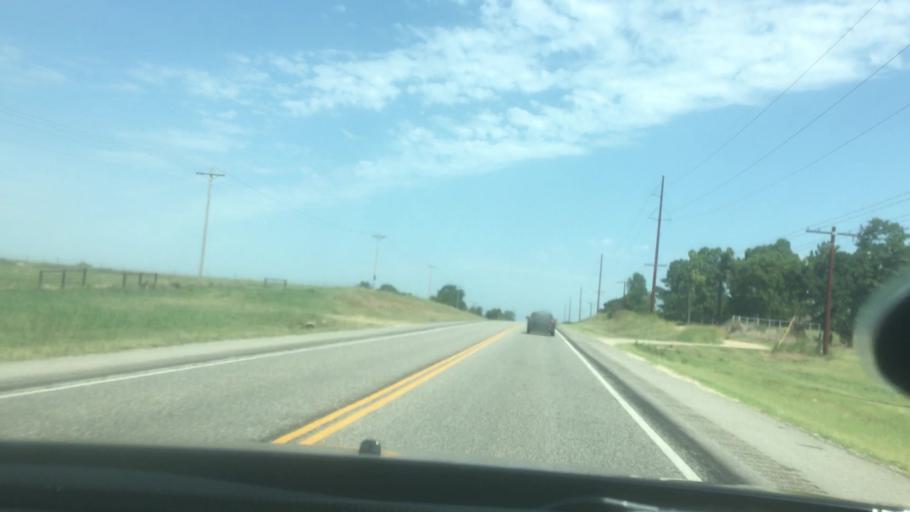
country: US
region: Oklahoma
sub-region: Seminole County
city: Konawa
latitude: 34.8573
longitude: -96.8199
